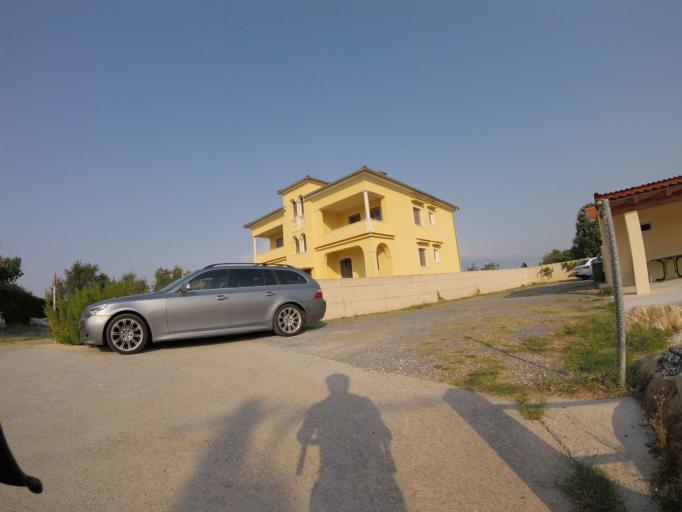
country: HR
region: Primorsko-Goranska
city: Lopar
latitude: 44.8340
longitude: 14.7289
